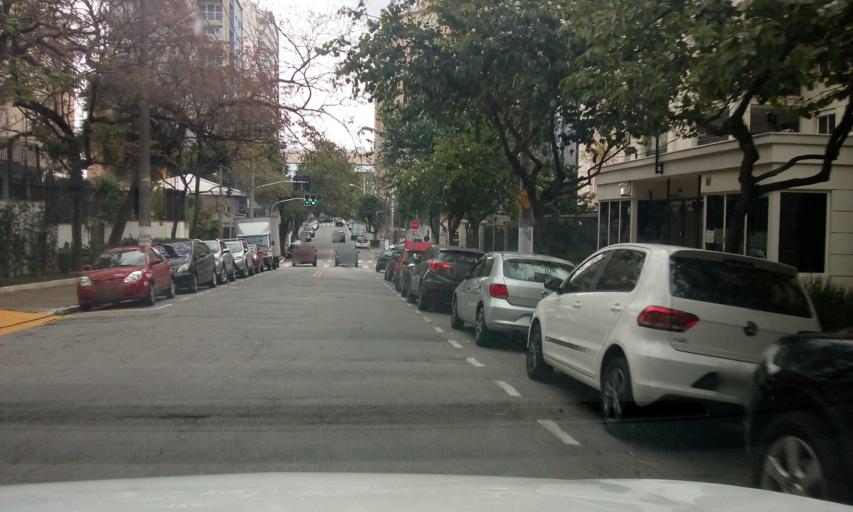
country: BR
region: Sao Paulo
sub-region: Sao Paulo
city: Sao Paulo
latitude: -23.6074
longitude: -46.6642
